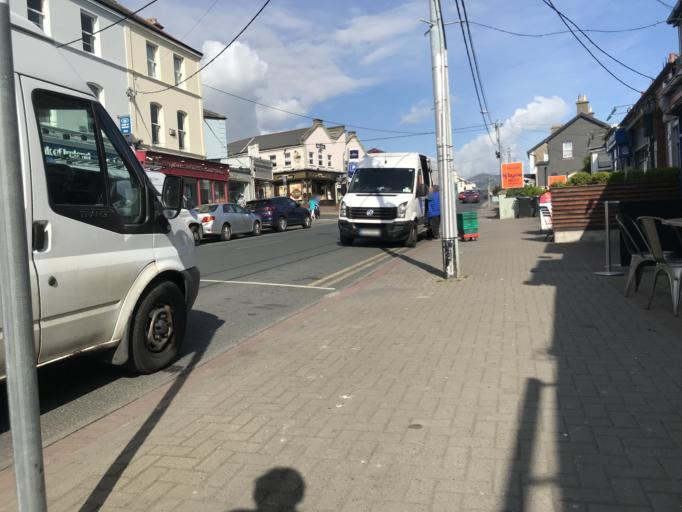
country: IE
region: Leinster
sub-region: Wicklow
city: Greystones
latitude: 53.1443
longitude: -6.0619
